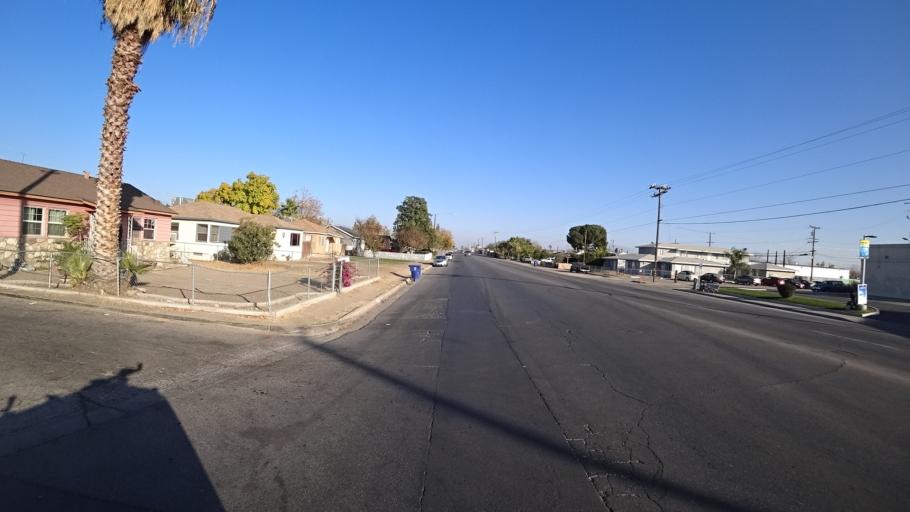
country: US
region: California
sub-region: Kern County
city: Bakersfield
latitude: 35.3395
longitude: -119.0181
